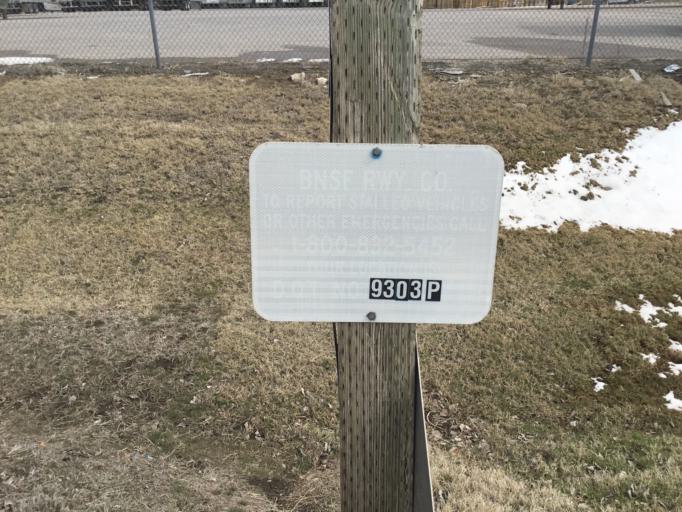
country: US
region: Kansas
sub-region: Sedgwick County
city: Wichita
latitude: 37.7452
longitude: -97.3305
